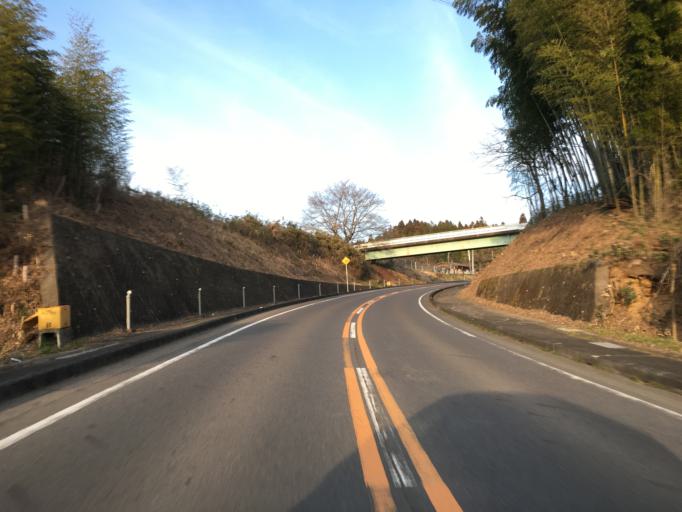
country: JP
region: Ibaraki
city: Daigo
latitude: 36.8185
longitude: 140.3717
